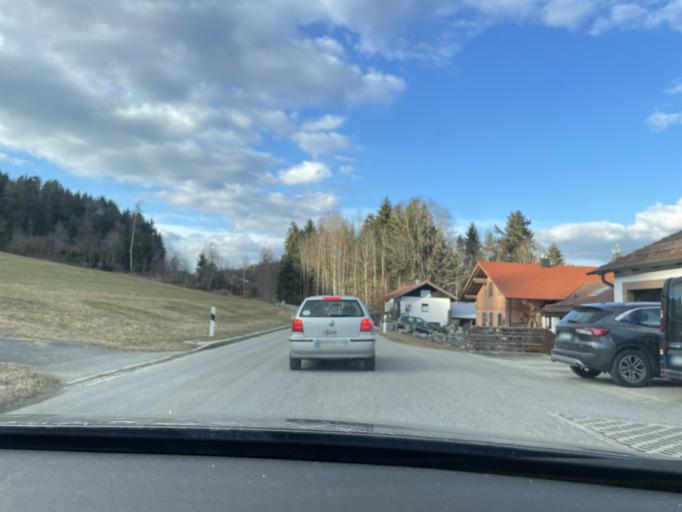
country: DE
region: Bavaria
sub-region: Lower Bavaria
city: Kollnburg
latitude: 49.0387
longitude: 12.8660
